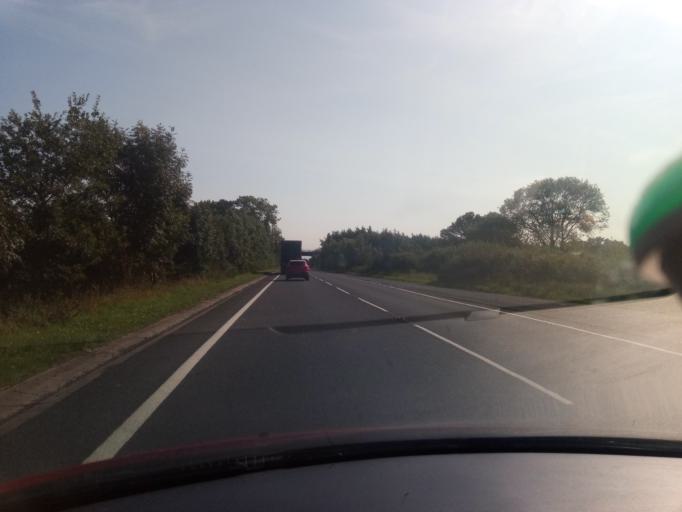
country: GB
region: England
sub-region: North Yorkshire
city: Easingwold
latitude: 54.1175
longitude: -1.2137
